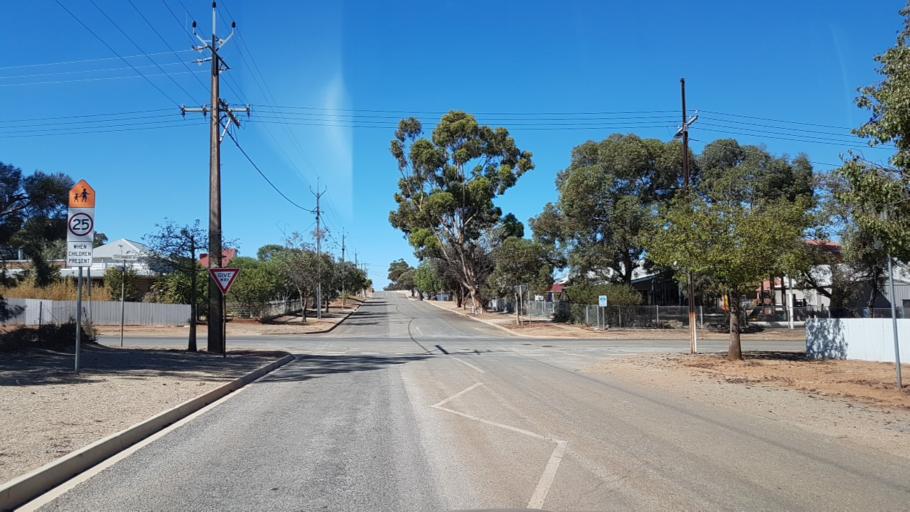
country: AU
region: South Australia
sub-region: Peterborough
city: Peterborough
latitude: -32.9706
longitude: 138.8314
